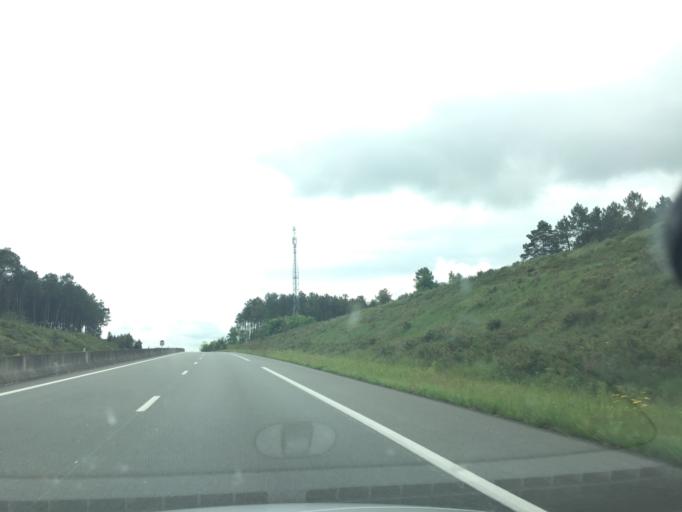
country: FR
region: Pays de la Loire
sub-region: Departement de la Sarthe
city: Luceau
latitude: 47.7084
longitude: 0.3483
